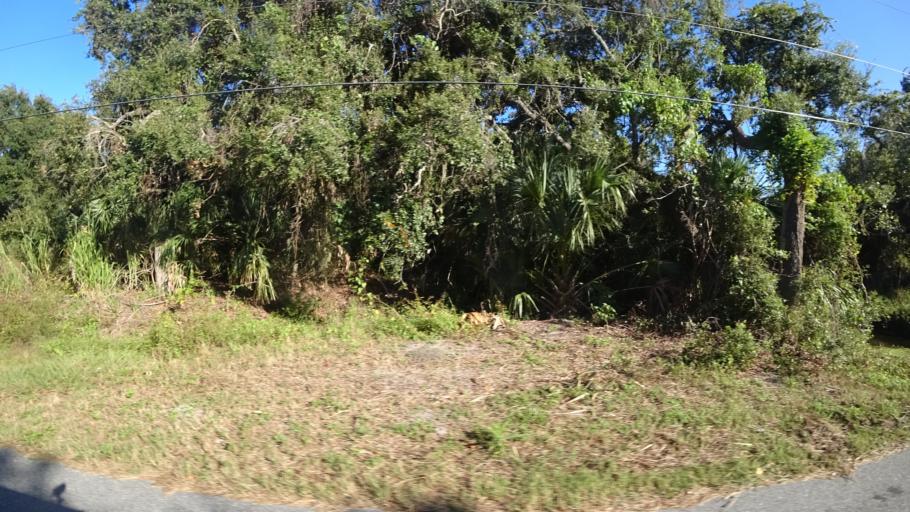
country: US
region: Florida
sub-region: Manatee County
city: Memphis
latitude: 27.6455
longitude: -82.5371
